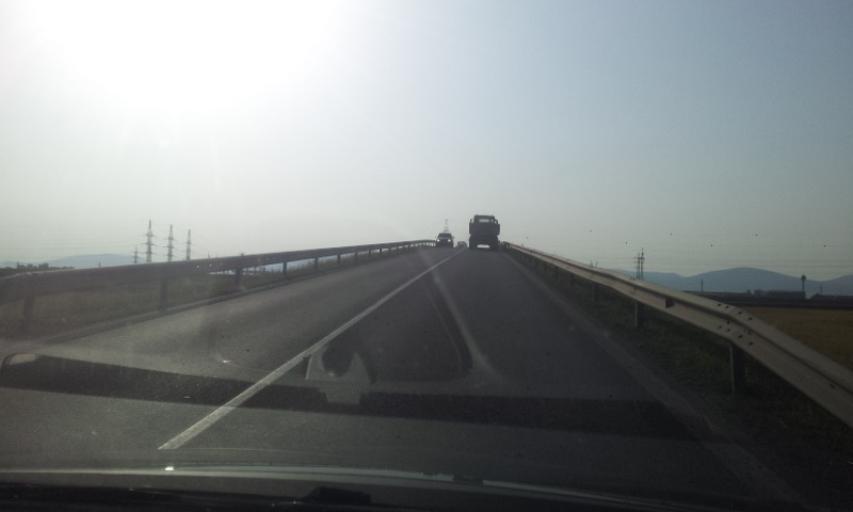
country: SK
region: Kosicky
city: Kosice
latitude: 48.6170
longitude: 21.2390
